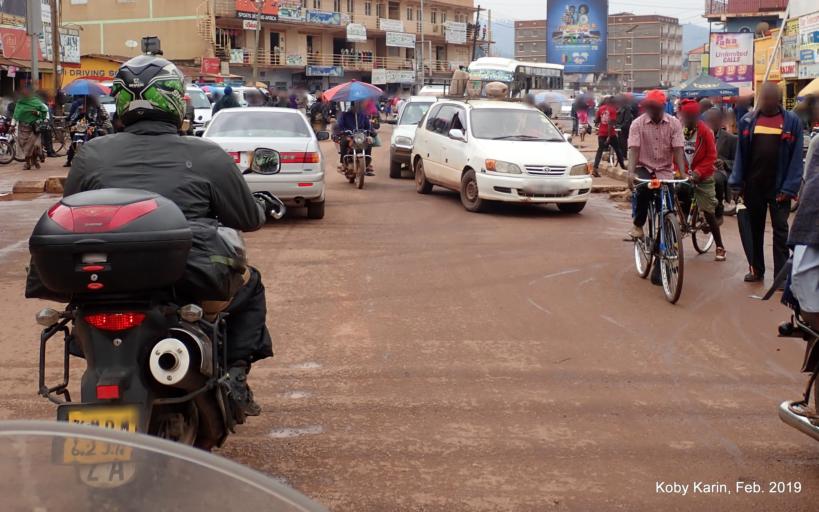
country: UG
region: Western Region
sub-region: Kabale District
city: Kabale
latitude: -1.2595
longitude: 29.9931
